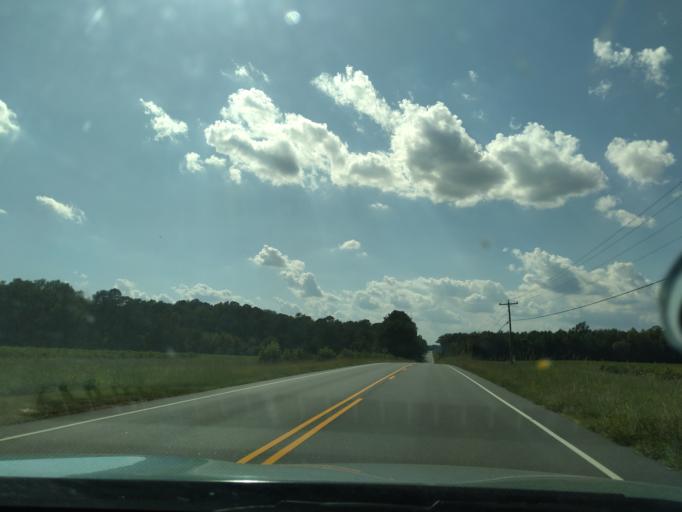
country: US
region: North Carolina
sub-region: Martin County
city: Robersonville
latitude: 35.8252
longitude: -77.2850
